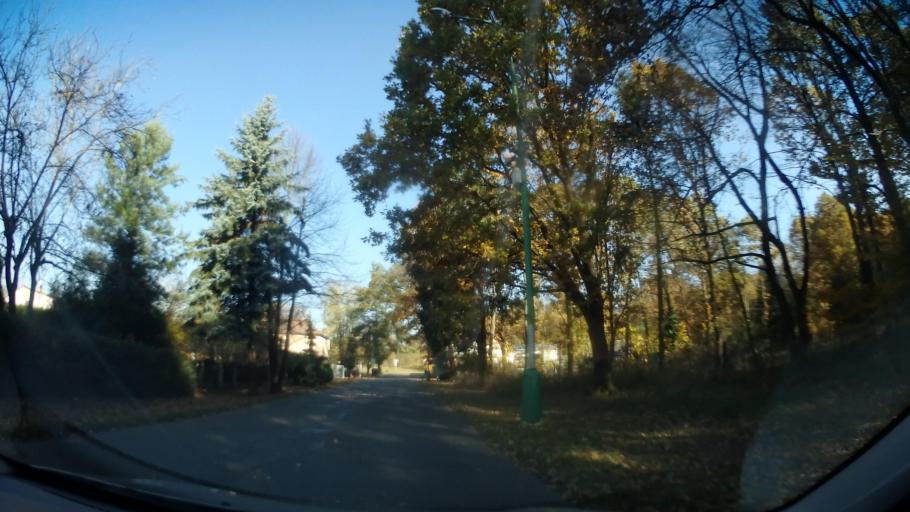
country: CZ
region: Kralovehradecky
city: Trebechovice pod Orebem
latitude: 50.1987
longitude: 16.0048
